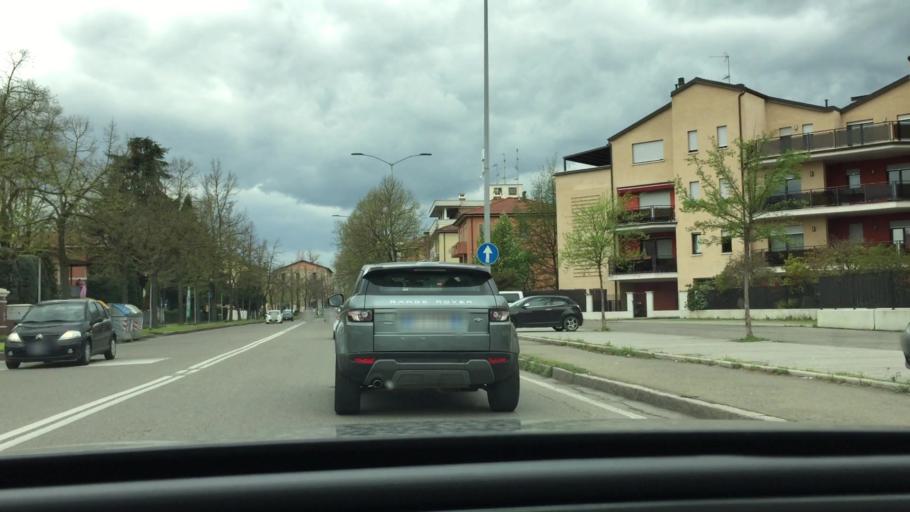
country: IT
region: Emilia-Romagna
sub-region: Provincia di Modena
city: Modena
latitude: 44.6310
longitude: 10.8997
